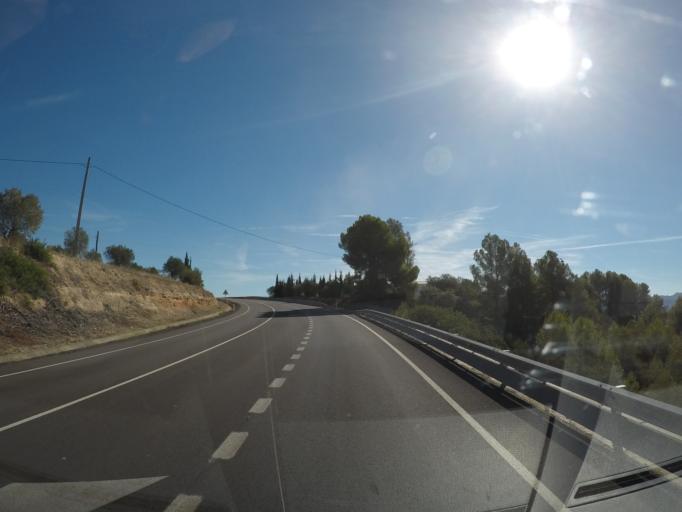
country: ES
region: Catalonia
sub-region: Provincia de Tarragona
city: Garcia
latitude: 41.1058
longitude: 0.6722
